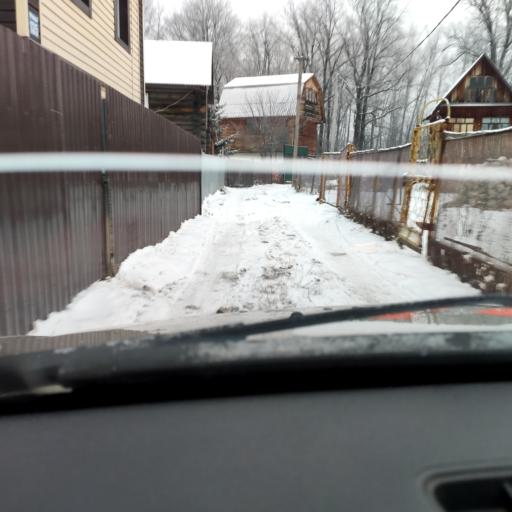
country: RU
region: Bashkortostan
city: Ufa
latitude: 54.6928
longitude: 55.8916
